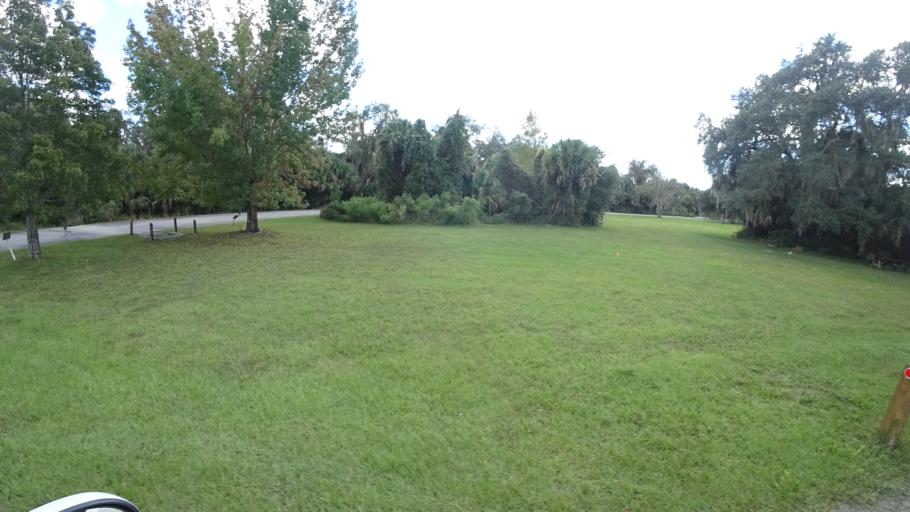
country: US
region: Florida
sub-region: Sarasota County
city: Lake Sarasota
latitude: 27.2403
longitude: -82.3153
